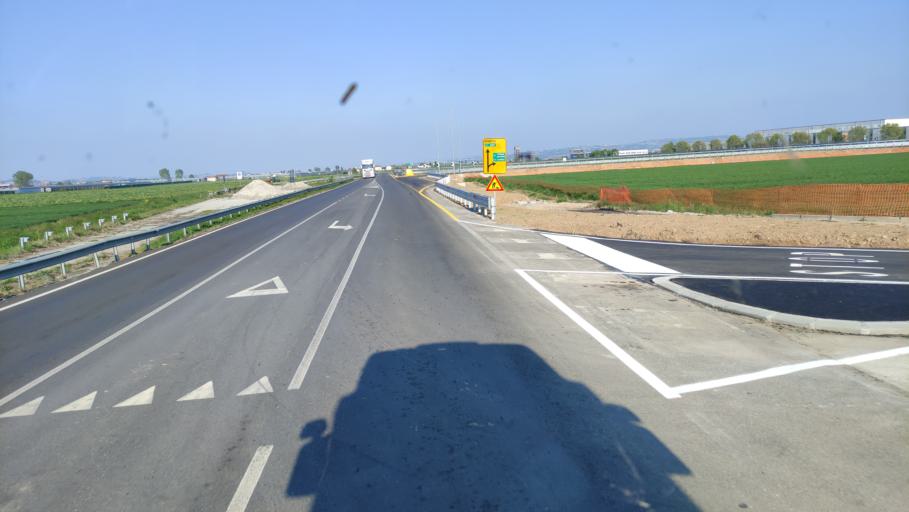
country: IT
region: Piedmont
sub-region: Provincia di Cuneo
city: Cervere
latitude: 44.6644
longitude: 7.7805
